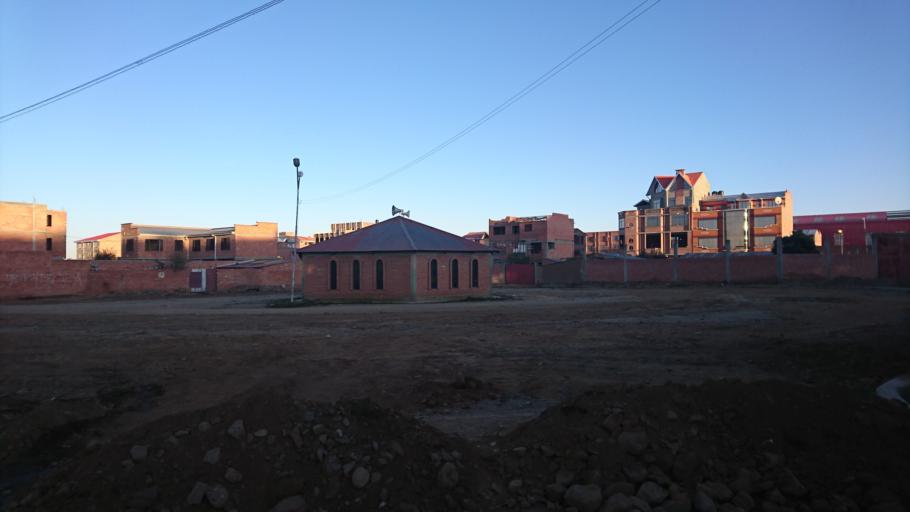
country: BO
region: La Paz
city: La Paz
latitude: -16.4997
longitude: -68.1887
